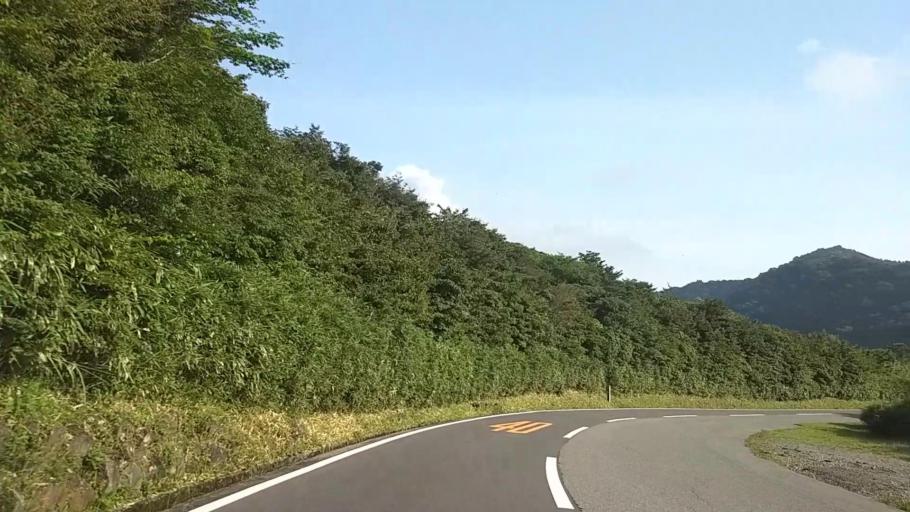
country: JP
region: Kanagawa
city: Hakone
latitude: 35.2094
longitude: 138.9877
